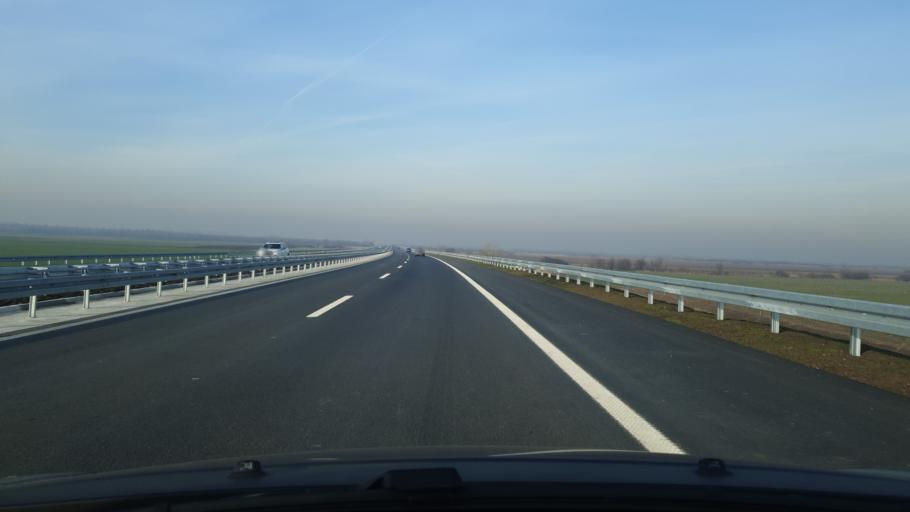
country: RS
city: Umka
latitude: 44.6923
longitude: 20.2673
